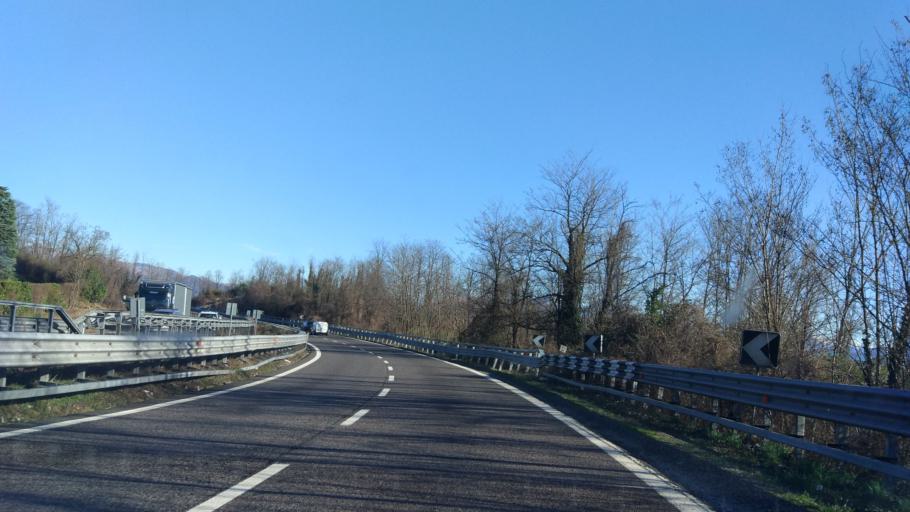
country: IT
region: Lombardy
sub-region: Provincia di Monza e Brianza
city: Briosco
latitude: 45.7015
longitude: 9.2315
